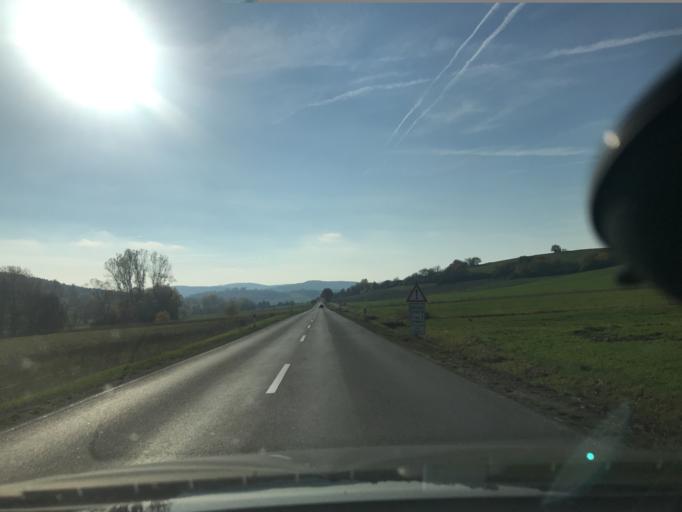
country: DE
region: Hesse
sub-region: Regierungsbezirk Kassel
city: Grossalmerode
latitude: 51.2110
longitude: 9.7932
